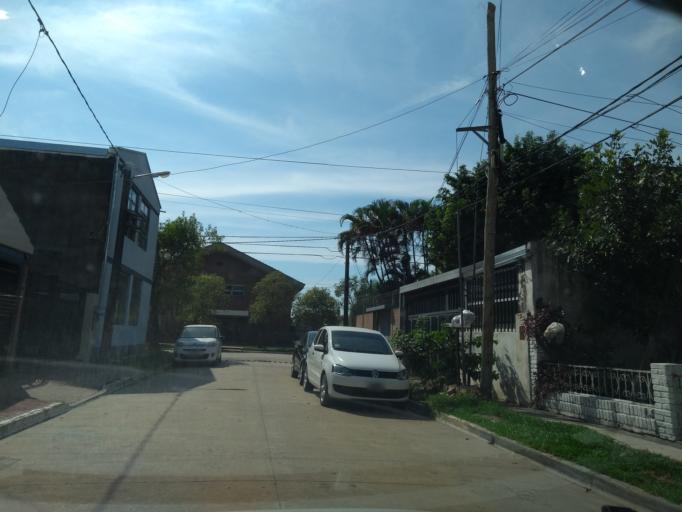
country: AR
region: Chaco
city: Resistencia
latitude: -27.4716
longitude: -58.9622
